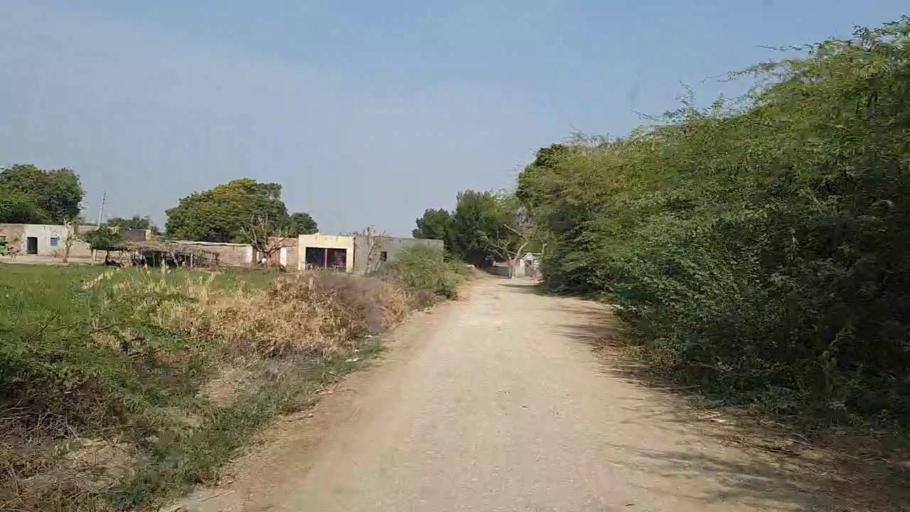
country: PK
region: Sindh
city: Mirwah Gorchani
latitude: 25.3433
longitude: 69.0632
